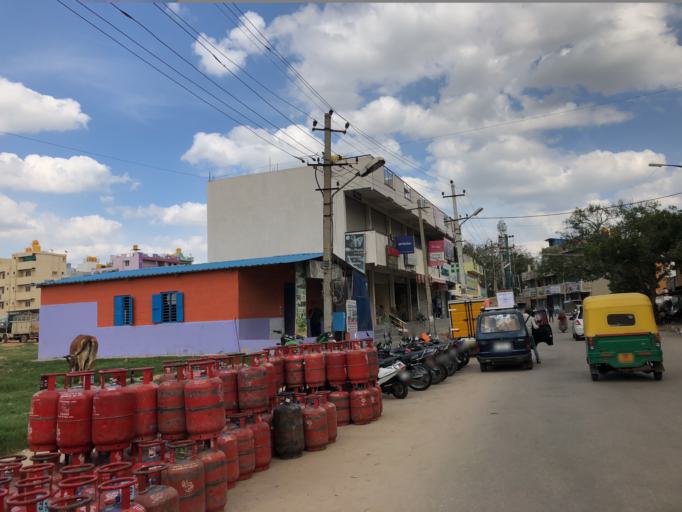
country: IN
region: Karnataka
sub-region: Bangalore Urban
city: Bangalore
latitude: 12.9919
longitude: 77.6890
